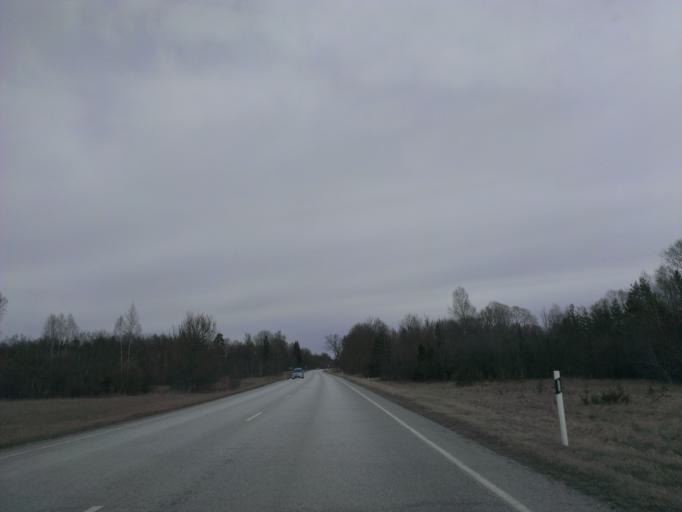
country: EE
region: Laeaene
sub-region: Lihula vald
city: Lihula
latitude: 58.6124
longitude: 23.5885
